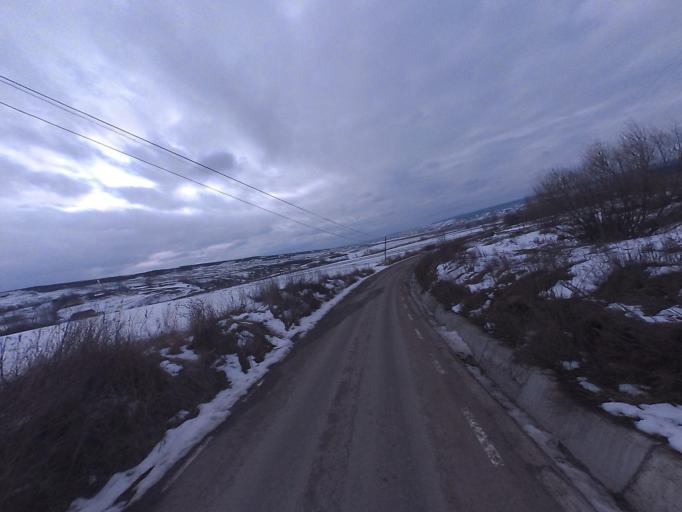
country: RO
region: Iasi
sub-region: Comuna Tibana
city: Tibana
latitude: 46.9843
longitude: 27.3527
